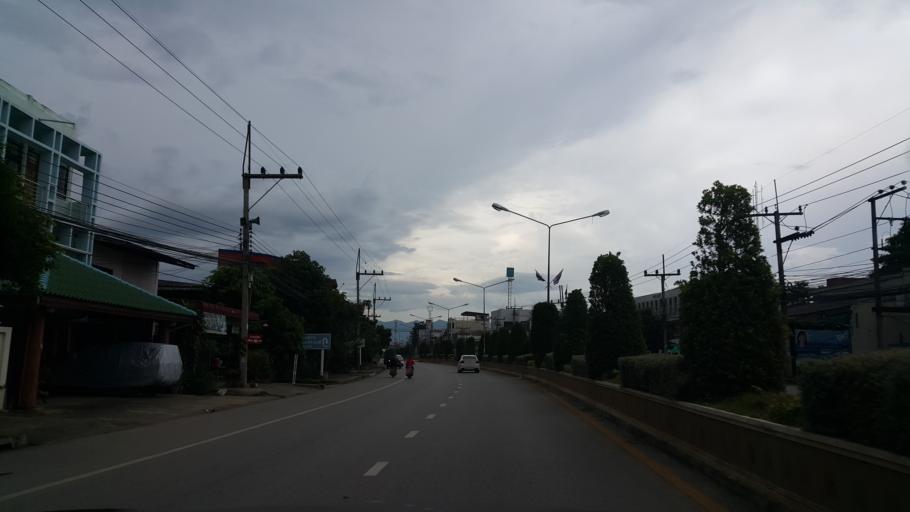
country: TH
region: Phayao
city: Dok Kham Tai
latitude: 19.1623
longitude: 99.9887
